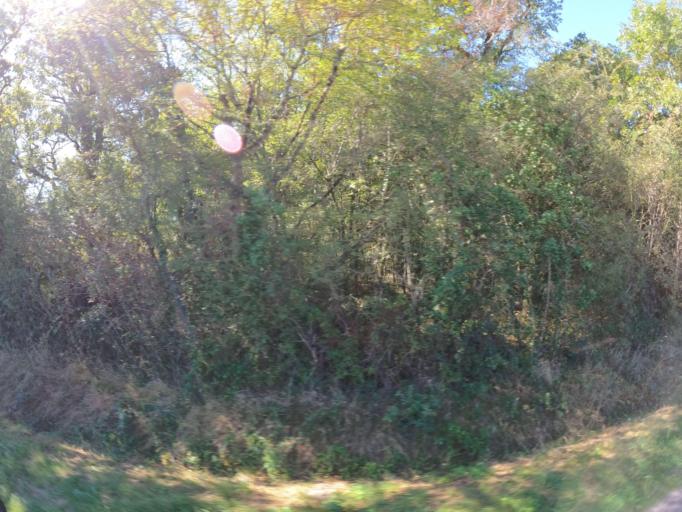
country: FR
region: Poitou-Charentes
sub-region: Departement de la Vienne
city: Lathus-Saint-Remy
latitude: 46.2779
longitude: 1.0159
